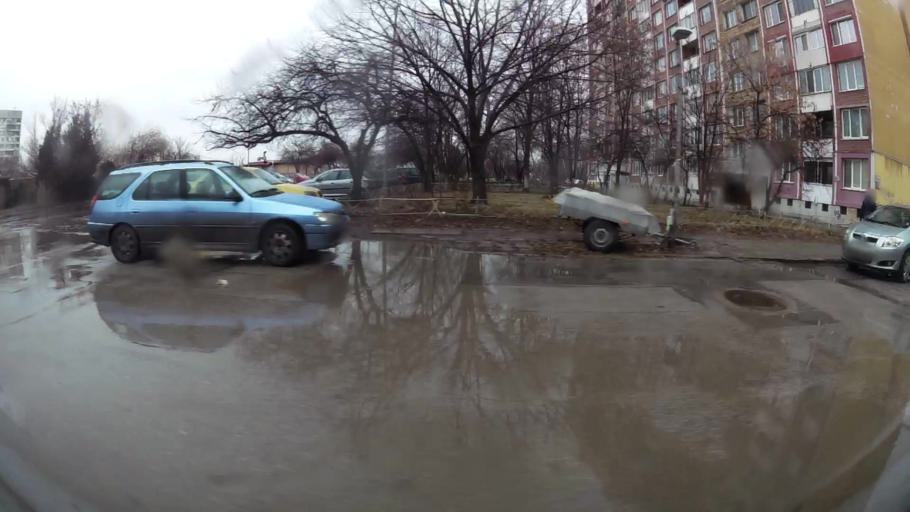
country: BG
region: Sofia-Capital
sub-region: Stolichna Obshtina
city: Sofia
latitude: 42.6611
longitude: 23.3986
